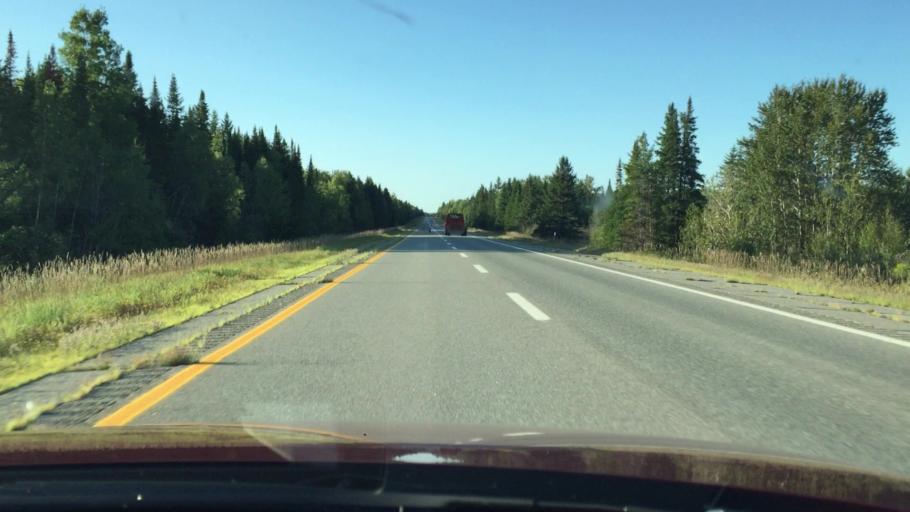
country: US
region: Maine
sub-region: Penobscot County
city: Patten
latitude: 45.8211
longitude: -68.4303
